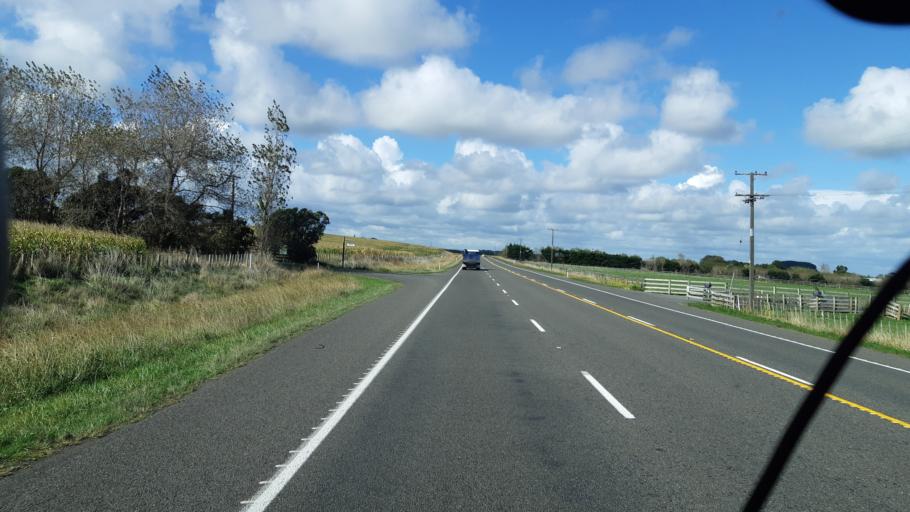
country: NZ
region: Manawatu-Wanganui
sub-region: Wanganui District
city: Wanganui
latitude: -39.9805
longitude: 175.1435
